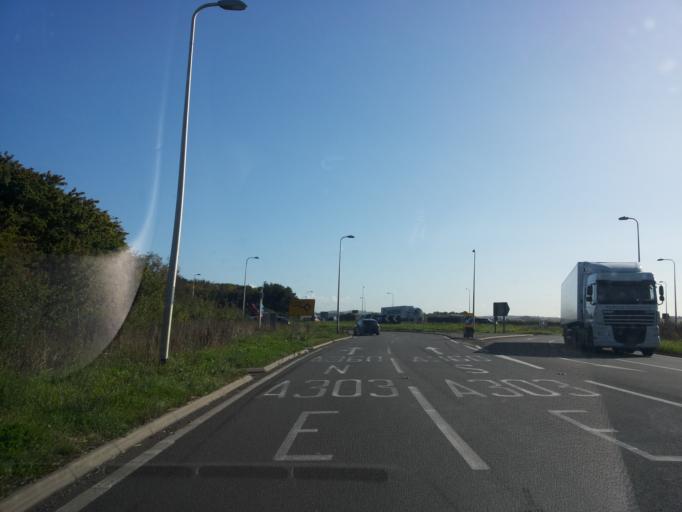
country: GB
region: England
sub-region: Wiltshire
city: Winterbourne Stoke
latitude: 51.1716
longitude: -1.8617
